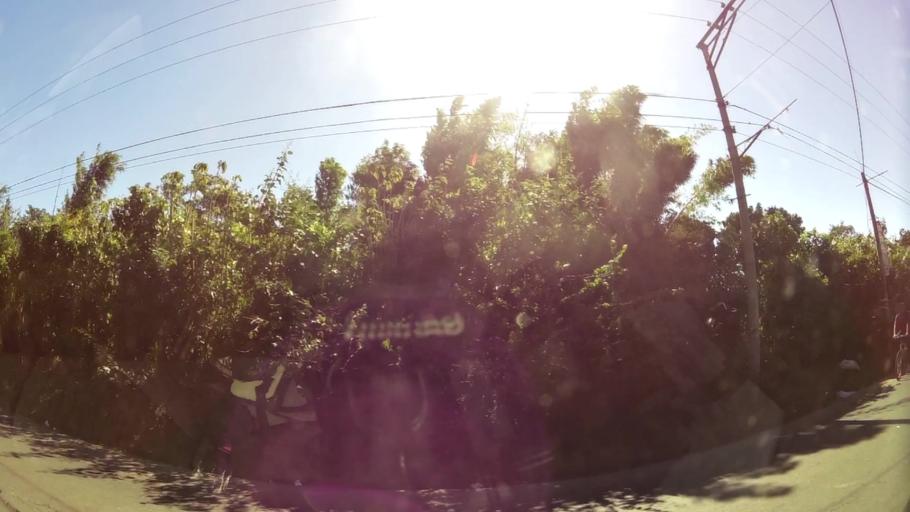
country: SV
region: Sonsonate
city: Juayua
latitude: 13.8406
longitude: -89.7515
